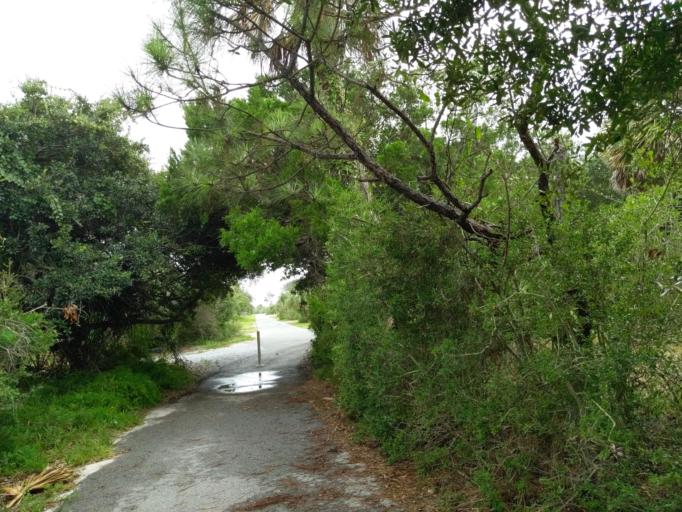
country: US
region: Florida
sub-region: Franklin County
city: Apalachicola
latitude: 29.6263
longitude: -84.9338
